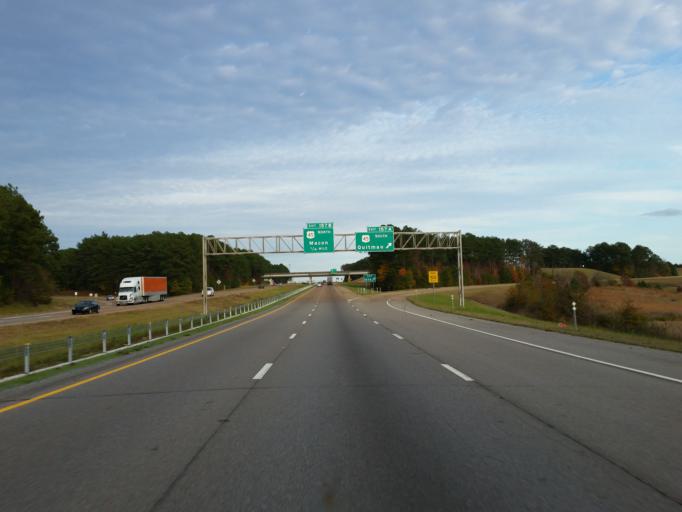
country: US
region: Mississippi
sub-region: Lauderdale County
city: Marion
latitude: 32.3821
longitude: -88.6426
